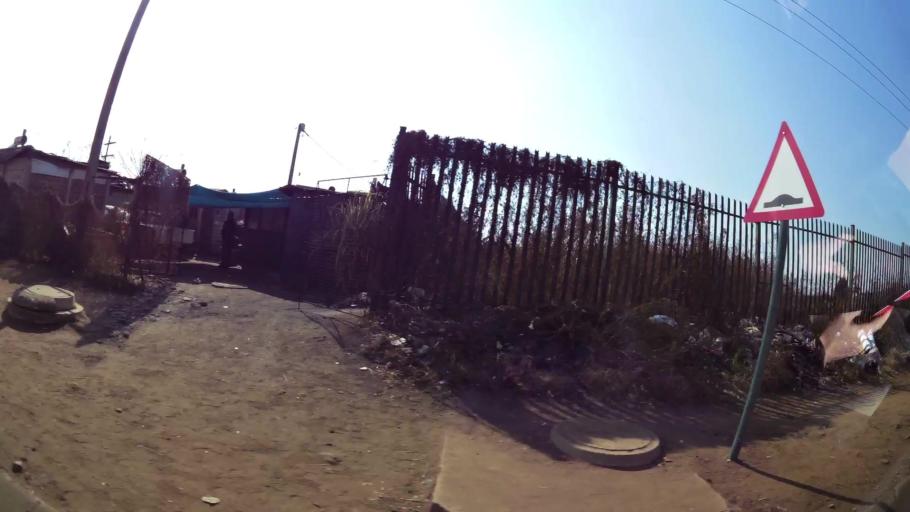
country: ZA
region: Gauteng
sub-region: Ekurhuleni Metropolitan Municipality
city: Springs
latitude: -26.1128
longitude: 28.4804
